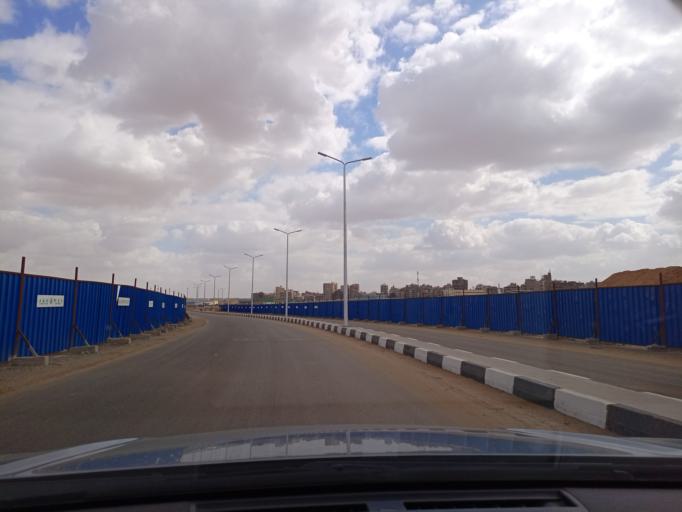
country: EG
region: Muhafazat al Qalyubiyah
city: Al Khankah
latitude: 30.1233
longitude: 31.3522
